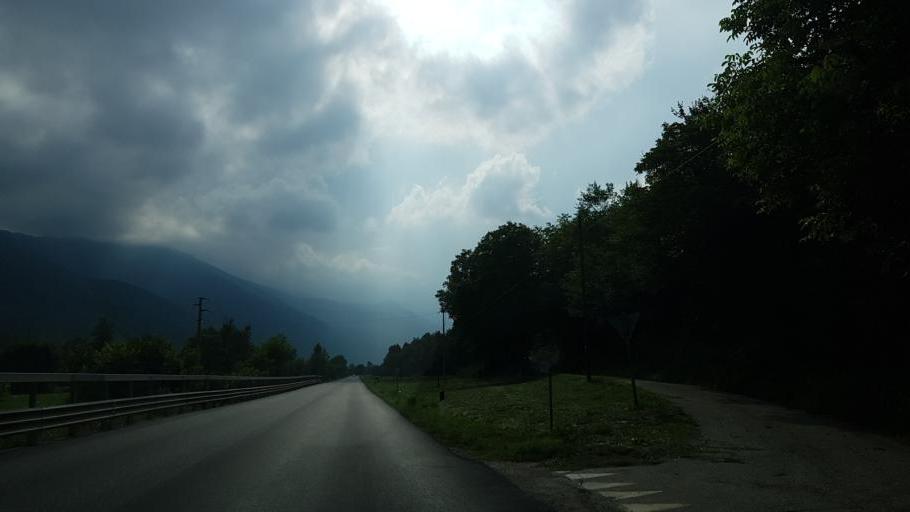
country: IT
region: Piedmont
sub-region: Provincia di Cuneo
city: Moiola
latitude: 44.3125
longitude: 7.3764
